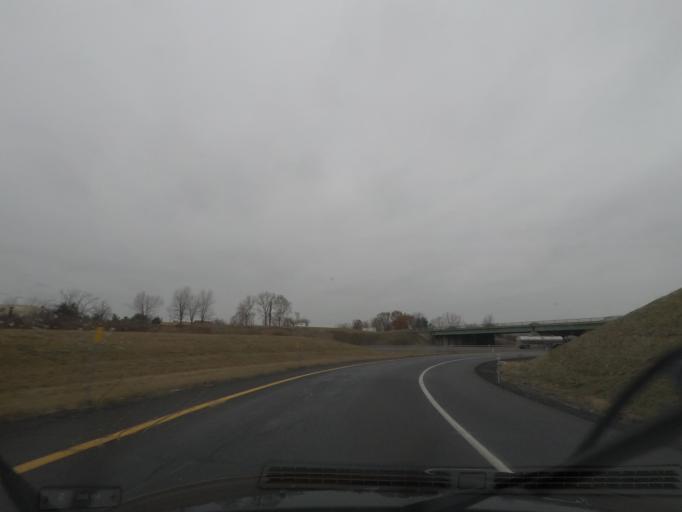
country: US
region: New York
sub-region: Rensselaer County
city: Hampton Manor
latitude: 42.6279
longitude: -73.6990
